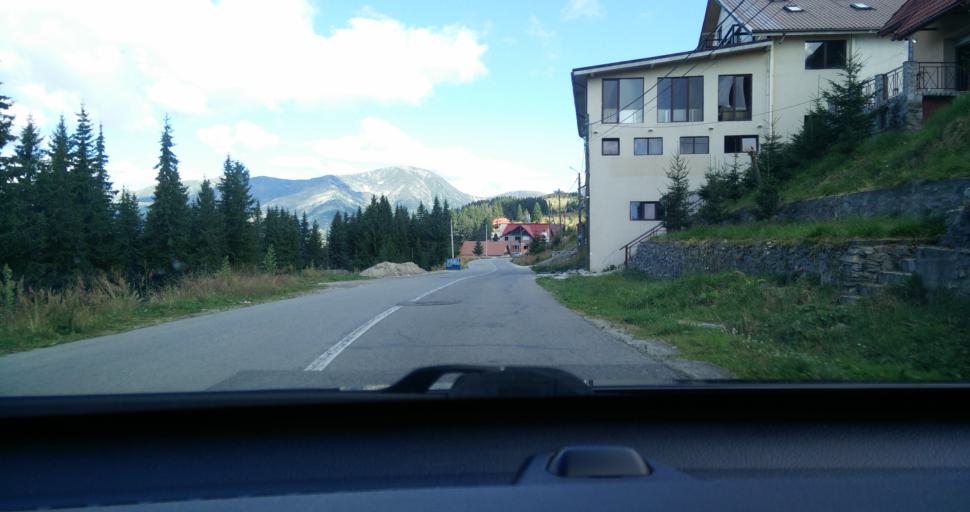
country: RO
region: Gorj
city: Novaci-Straini
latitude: 45.2889
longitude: 23.6904
